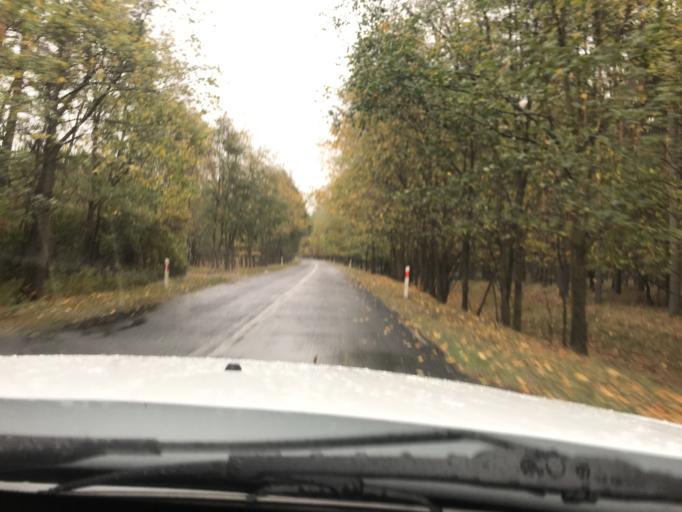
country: PL
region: West Pomeranian Voivodeship
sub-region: Powiat gryfinski
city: Moryn
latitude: 52.7735
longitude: 14.3583
